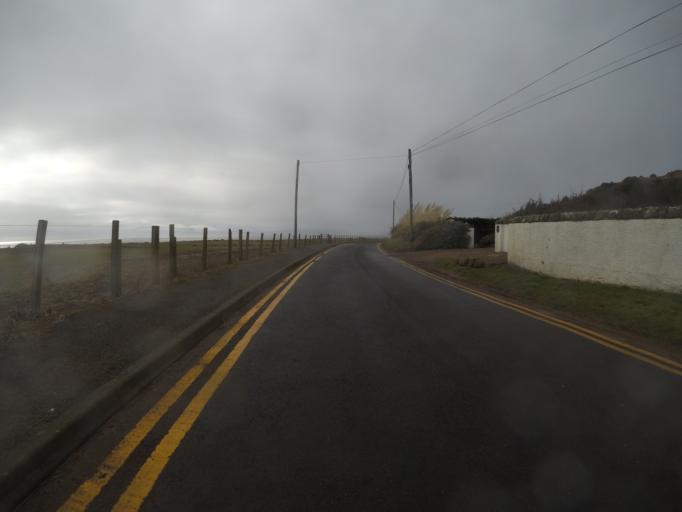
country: GB
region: Scotland
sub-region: North Ayrshire
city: West Kilbride
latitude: 55.6974
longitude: -4.8983
